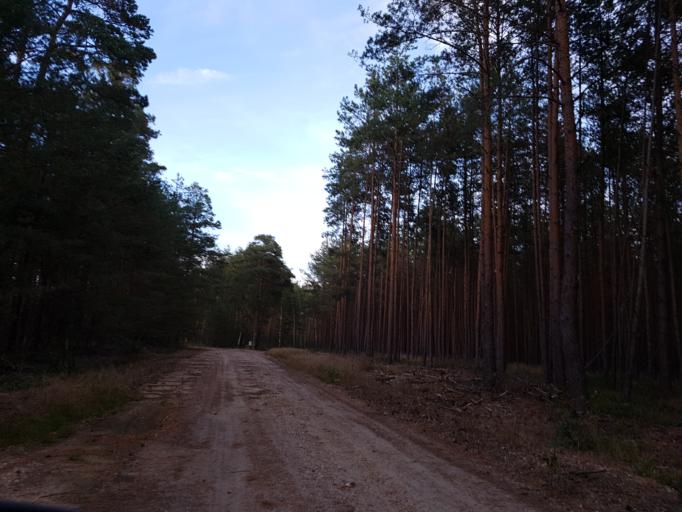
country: DE
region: Brandenburg
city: Trobitz
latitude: 51.5597
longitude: 13.4520
